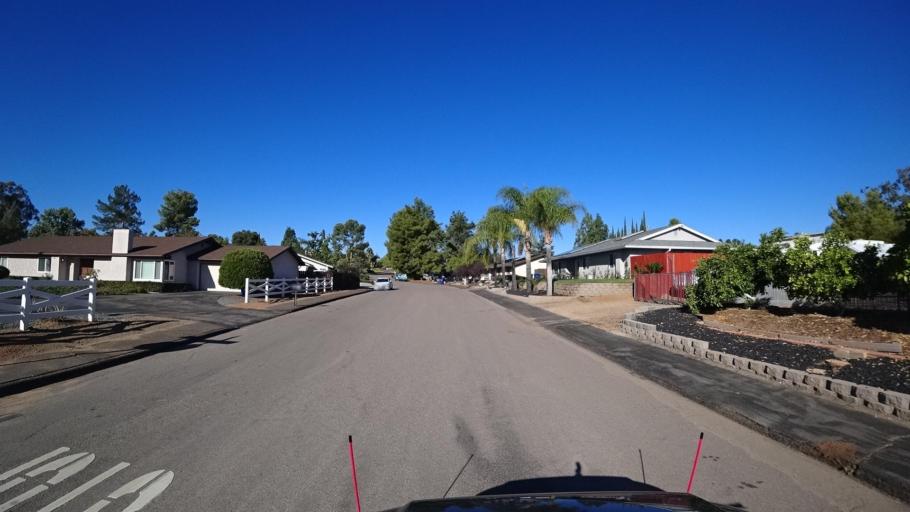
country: US
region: California
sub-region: San Diego County
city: Alpine
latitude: 32.8309
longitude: -116.7540
